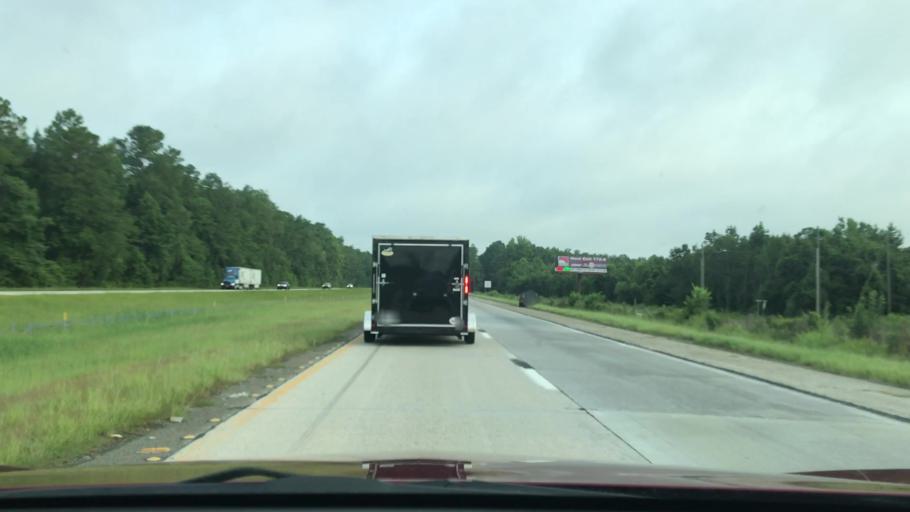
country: US
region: South Carolina
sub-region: Orangeburg County
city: Holly Hill
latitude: 33.2451
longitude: -80.4639
